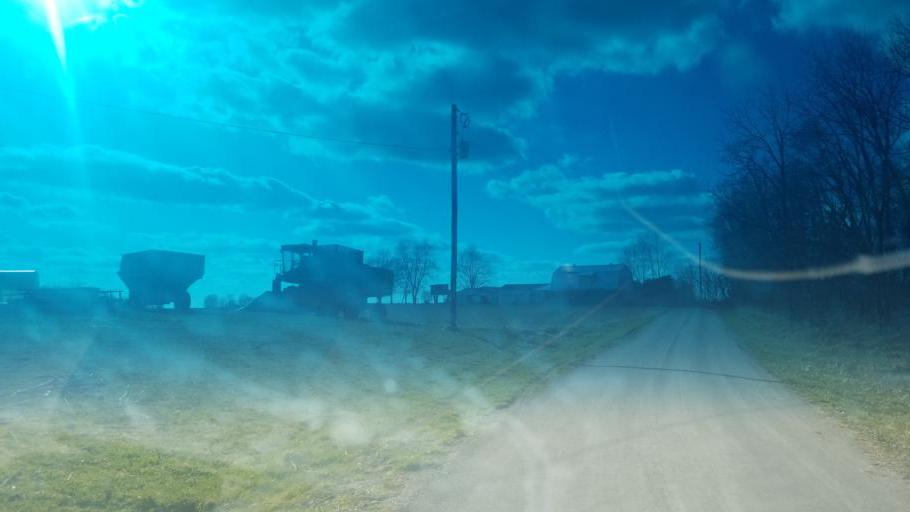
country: US
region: Ohio
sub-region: Highland County
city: Greenfield
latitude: 39.3000
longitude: -83.4370
